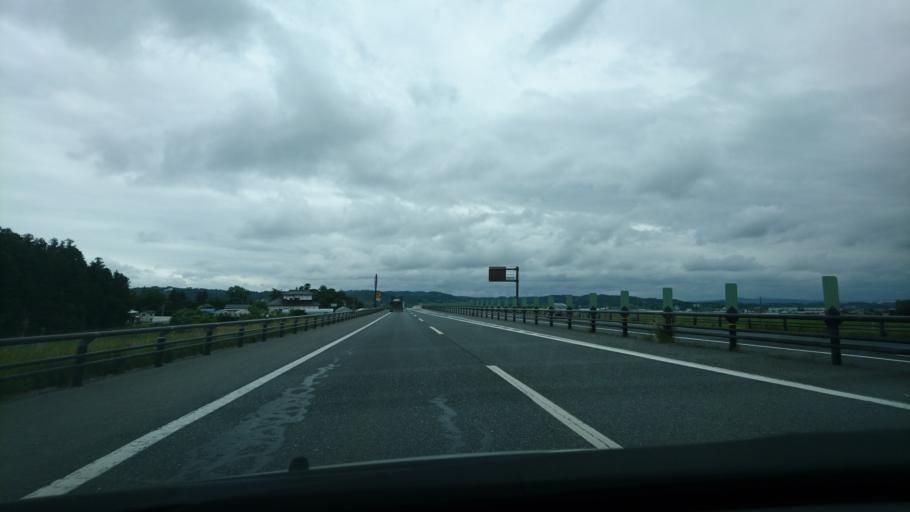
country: JP
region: Miyagi
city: Wakuya
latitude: 38.6700
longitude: 141.2656
